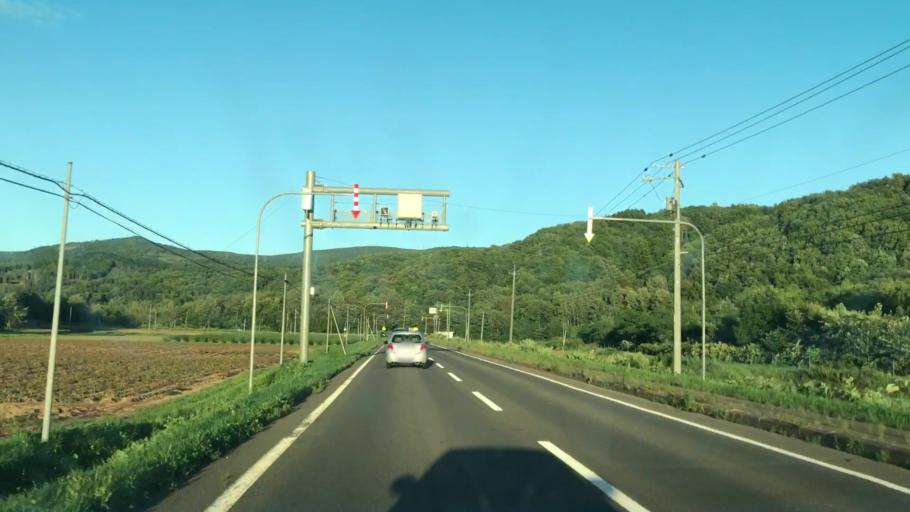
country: JP
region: Hokkaido
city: Niseko Town
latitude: 42.8003
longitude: 140.9842
